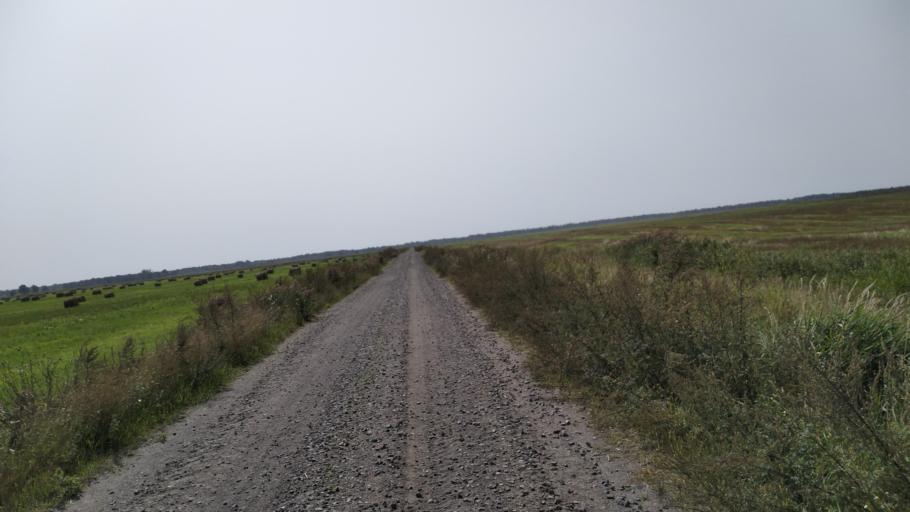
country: BY
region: Brest
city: Davyd-Haradok
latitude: 51.9920
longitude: 27.1762
